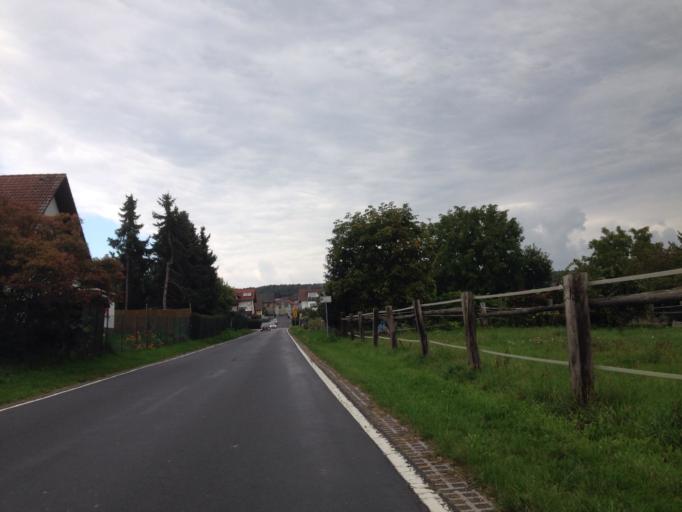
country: DE
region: Hesse
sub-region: Regierungsbezirk Giessen
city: Alten Buseck
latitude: 50.6169
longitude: 8.7529
